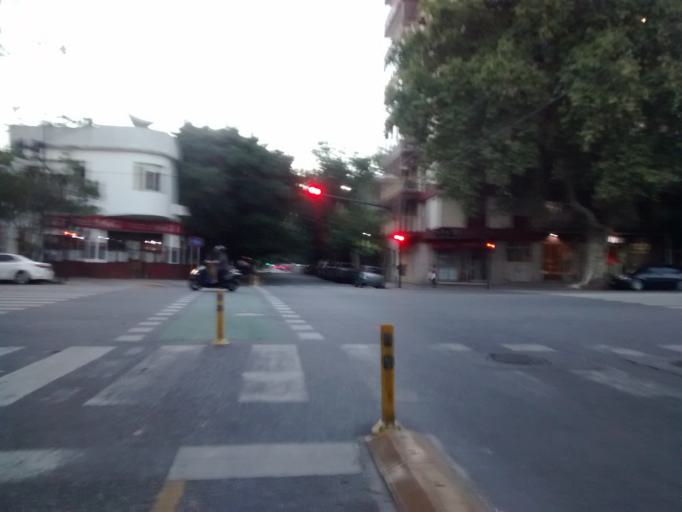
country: AR
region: Buenos Aires F.D.
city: Colegiales
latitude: -34.6028
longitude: -58.4493
